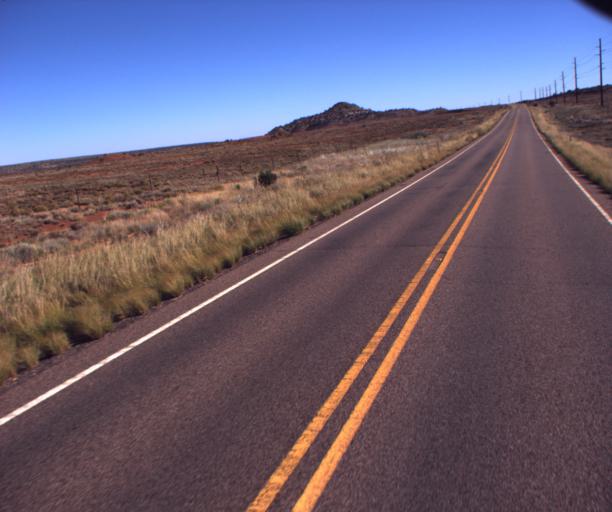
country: US
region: Arizona
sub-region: Navajo County
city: Taylor
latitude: 34.4927
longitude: -110.2184
